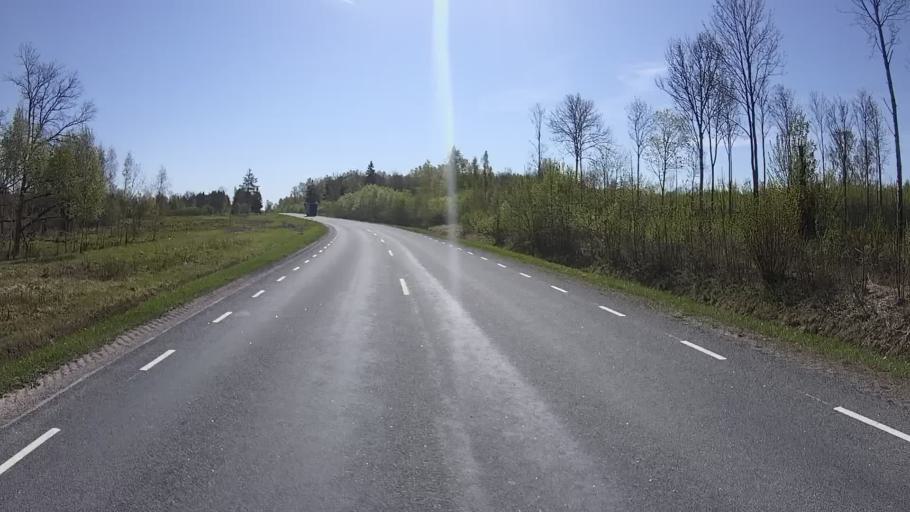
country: EE
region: Laeaene
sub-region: Lihula vald
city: Lihula
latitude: 58.5506
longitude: 23.9882
